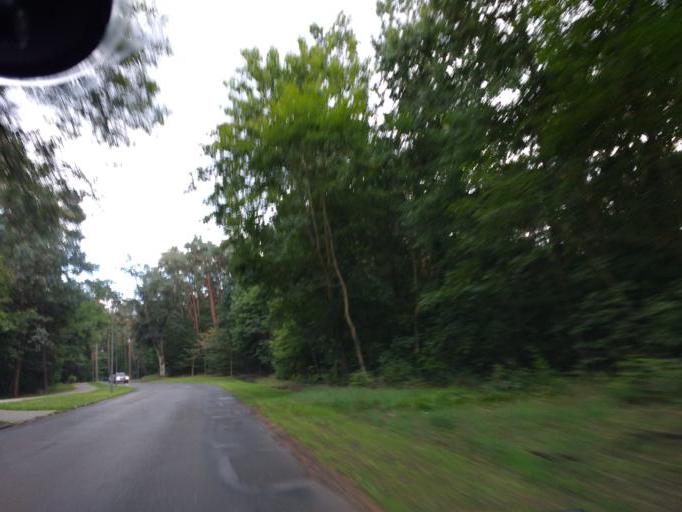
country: DE
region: Brandenburg
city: Bad Saarow
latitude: 52.2791
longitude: 14.0391
